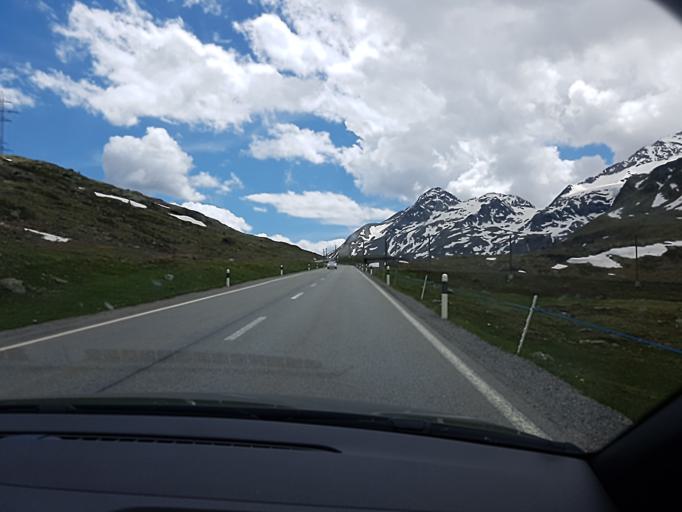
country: CH
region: Grisons
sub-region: Bernina District
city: Poschiavo
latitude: 46.4257
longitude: 9.9998
